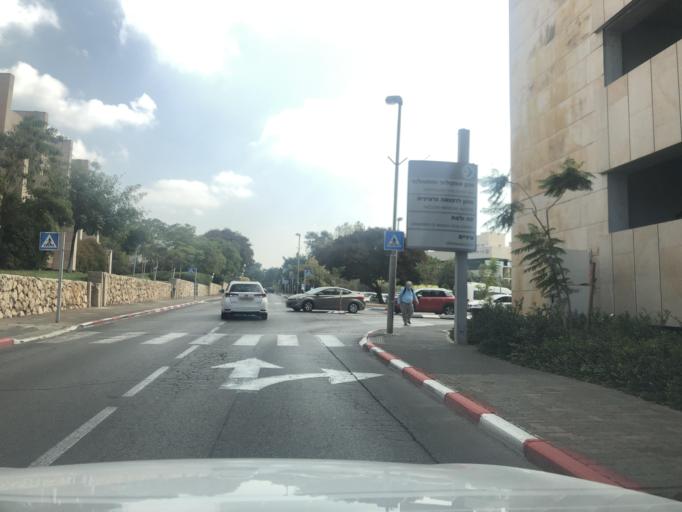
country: IL
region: Tel Aviv
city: Or Yehuda
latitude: 32.0471
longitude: 34.8455
